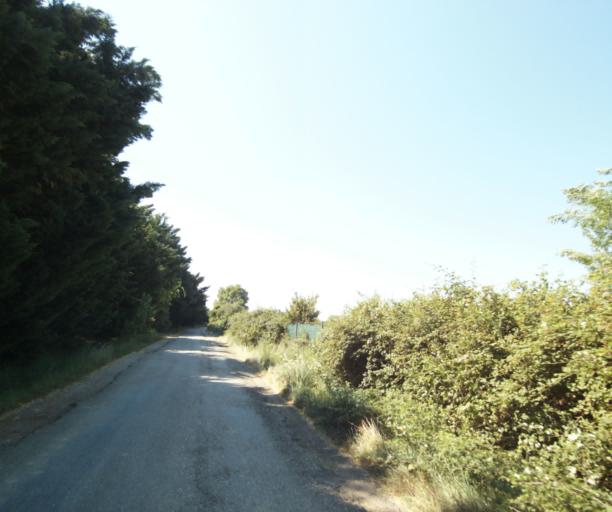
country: FR
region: Languedoc-Roussillon
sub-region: Departement de l'Herault
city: Marsillargues
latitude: 43.6529
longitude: 4.1659
